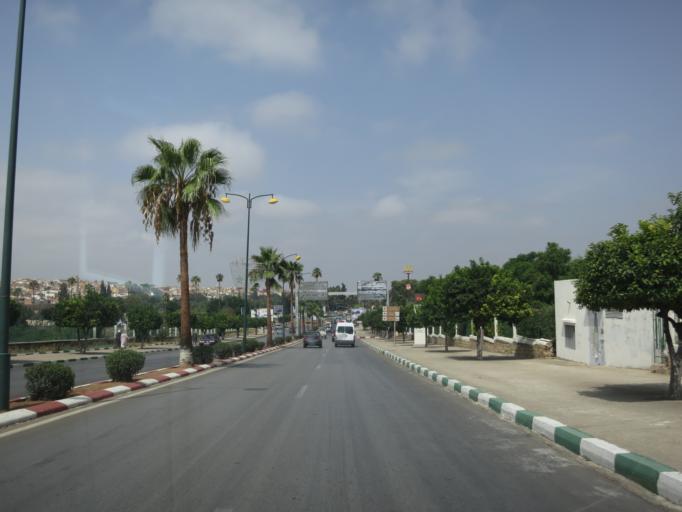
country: MA
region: Meknes-Tafilalet
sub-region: Meknes
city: Meknes
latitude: 33.8946
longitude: -5.5535
